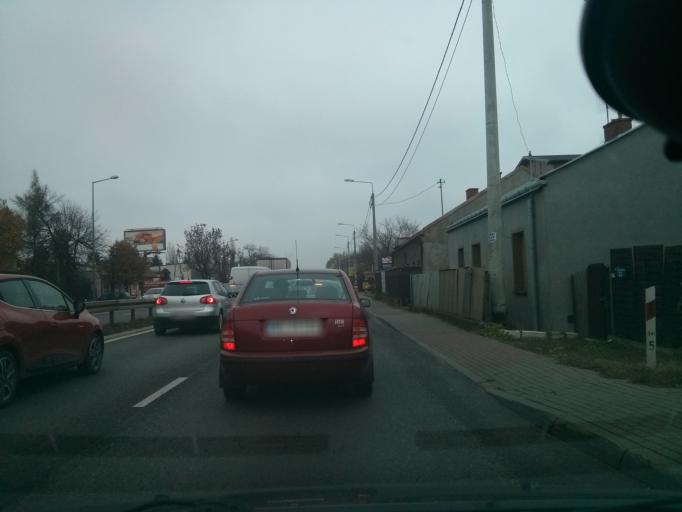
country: PL
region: Masovian Voivodeship
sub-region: Powiat pruszkowski
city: Raszyn
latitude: 52.1564
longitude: 20.9230
